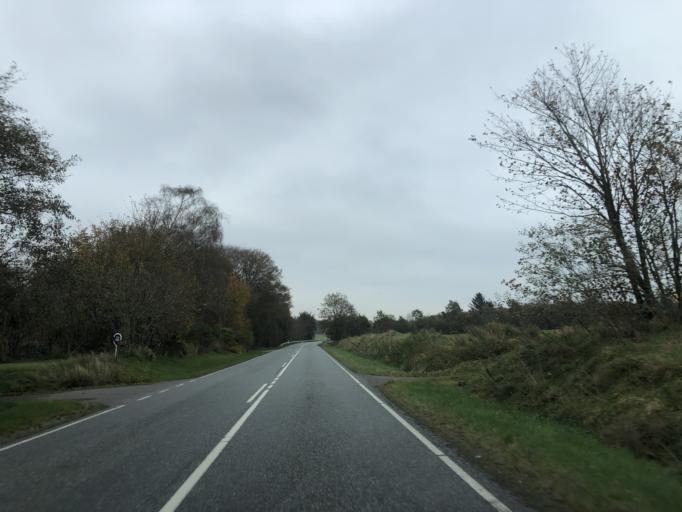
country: DK
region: Central Jutland
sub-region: Holstebro Kommune
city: Ulfborg
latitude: 56.1987
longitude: 8.4061
